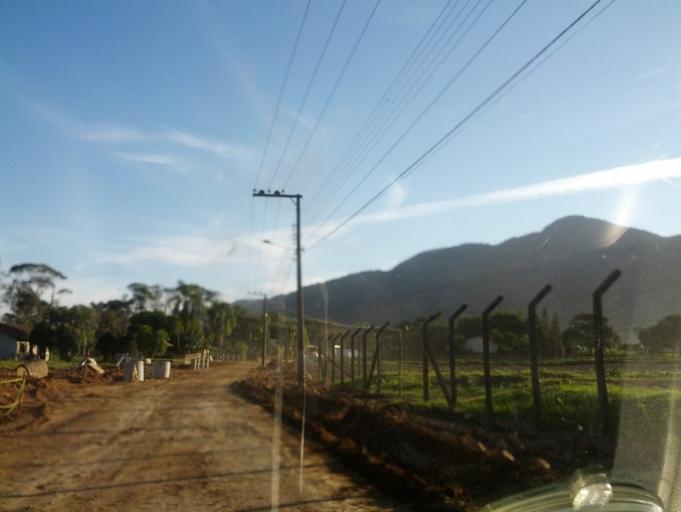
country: BR
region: Santa Catarina
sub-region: Indaial
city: Indaial
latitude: -26.9092
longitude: -49.2659
